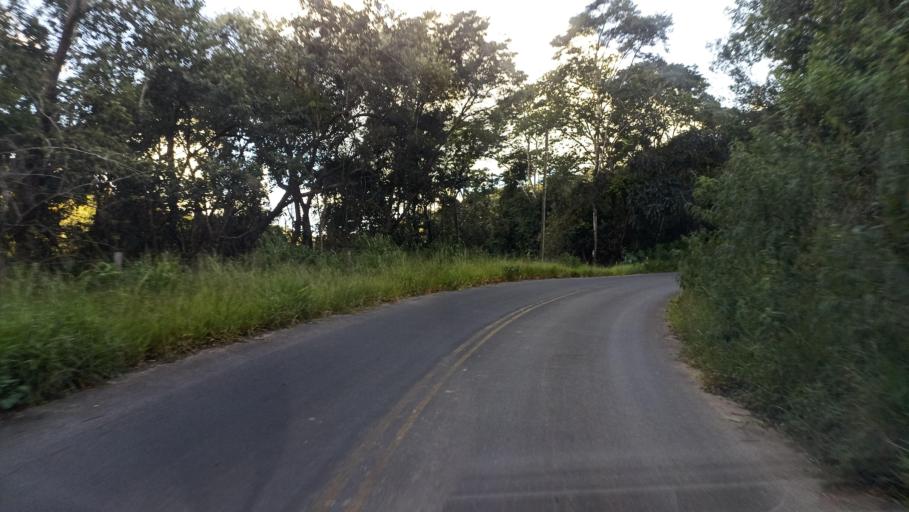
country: BR
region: Minas Gerais
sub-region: Ouro Preto
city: Ouro Preto
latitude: -20.3145
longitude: -43.6157
